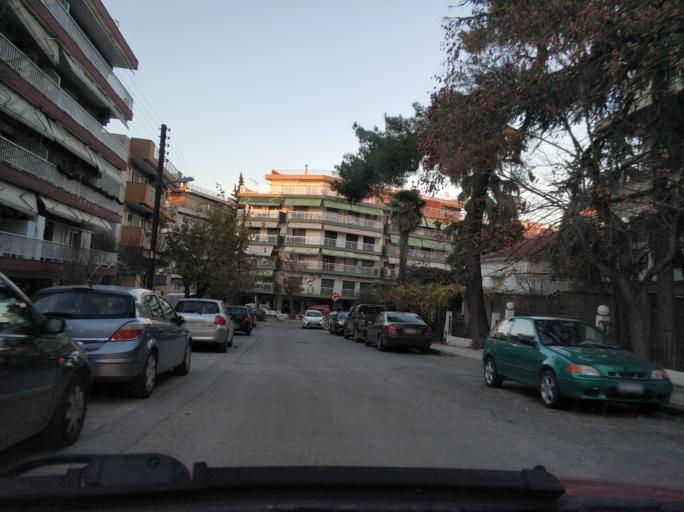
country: GR
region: Central Macedonia
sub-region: Nomos Thessalonikis
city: Pylaia
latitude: 40.5973
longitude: 22.9729
